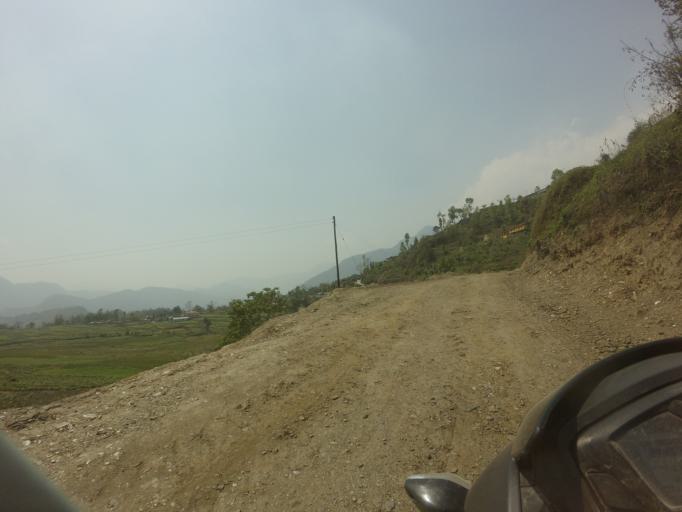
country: NP
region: Western Region
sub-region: Gandaki Zone
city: Pokhara
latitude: 28.3091
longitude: 83.9648
